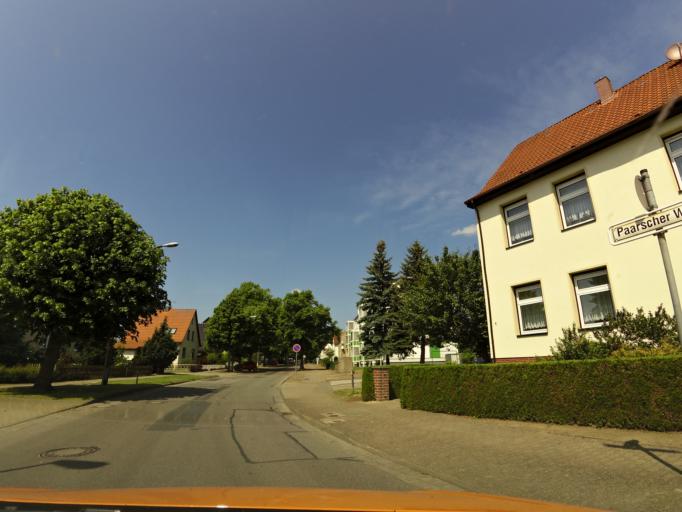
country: DE
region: Mecklenburg-Vorpommern
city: Parchim
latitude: 53.4274
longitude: 11.8603
